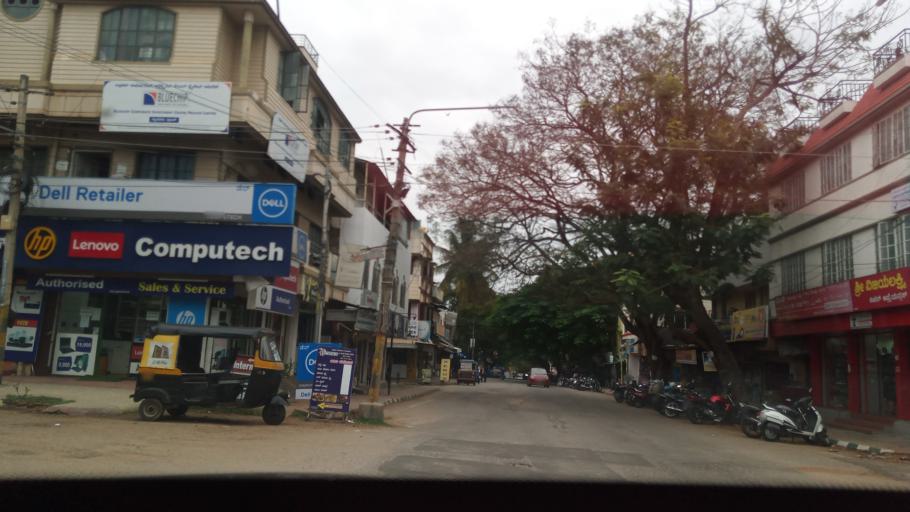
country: IN
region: Karnataka
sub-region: Mysore
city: Mysore
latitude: 12.3018
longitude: 76.6272
